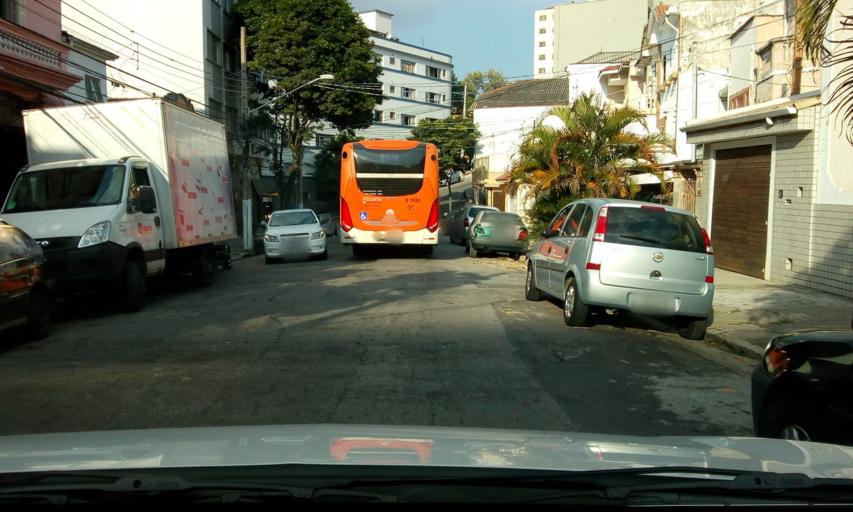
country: BR
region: Sao Paulo
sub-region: Sao Paulo
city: Sao Paulo
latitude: -23.5644
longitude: -46.6275
